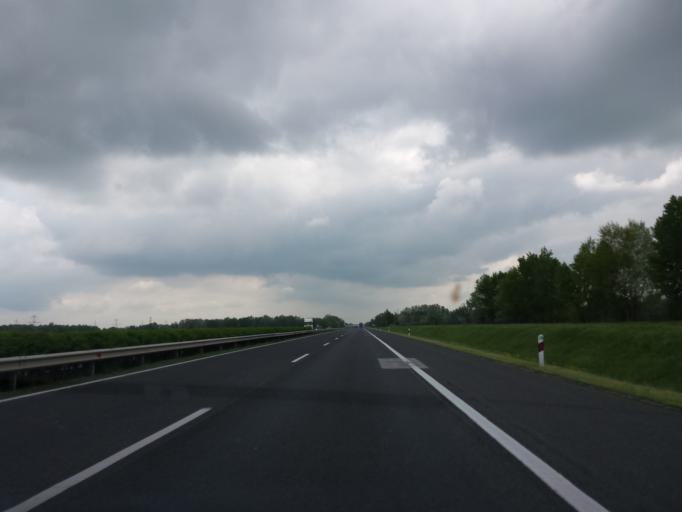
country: HU
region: Gyor-Moson-Sopron
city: Otteveny
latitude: 47.7240
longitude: 17.4567
